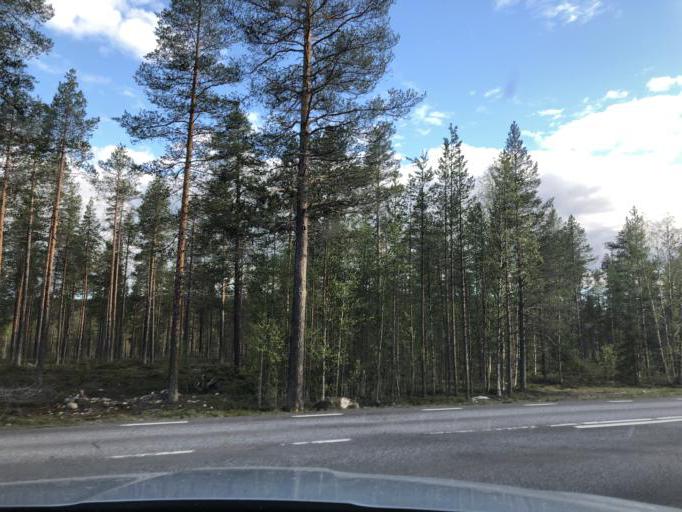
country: SE
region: Norrbotten
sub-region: Arvidsjaurs Kommun
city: Arvidsjaur
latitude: 65.6122
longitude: 19.0620
